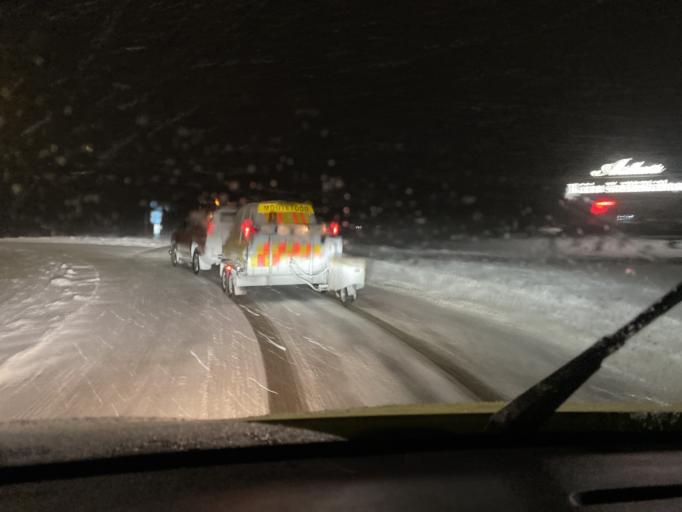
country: EE
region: Harju
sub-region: Kuusalu vald
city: Kuusalu
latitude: 59.4467
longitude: 25.3754
